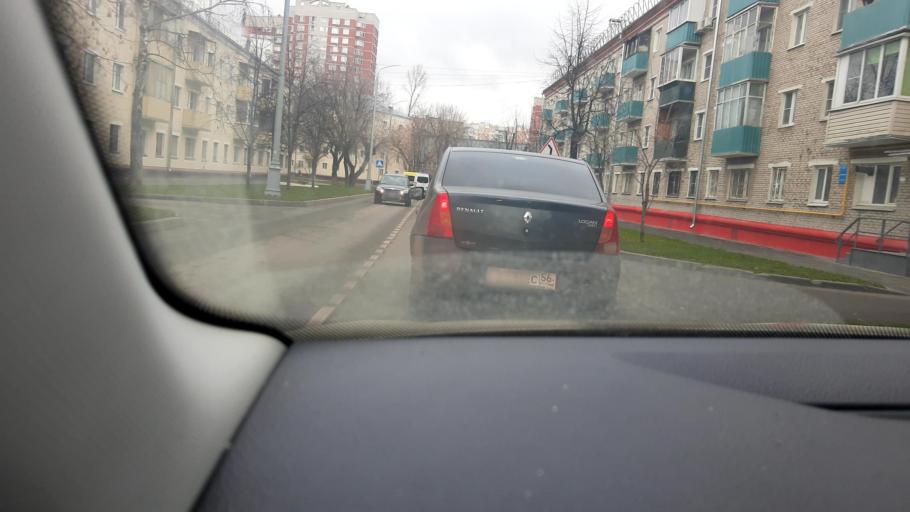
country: RU
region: Moskovskaya
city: Shcherbinka
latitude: 55.5034
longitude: 37.5648
